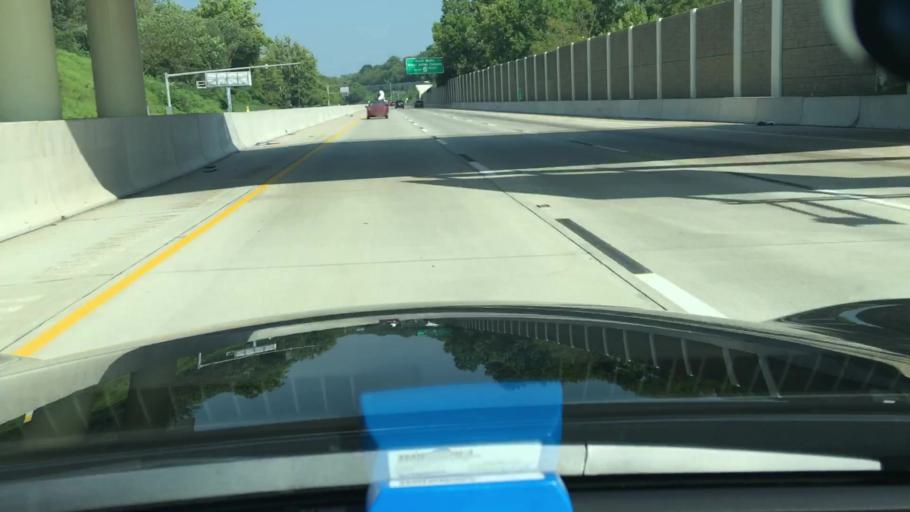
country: US
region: Pennsylvania
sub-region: Chester County
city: Malvern
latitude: 40.0518
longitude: -75.5551
